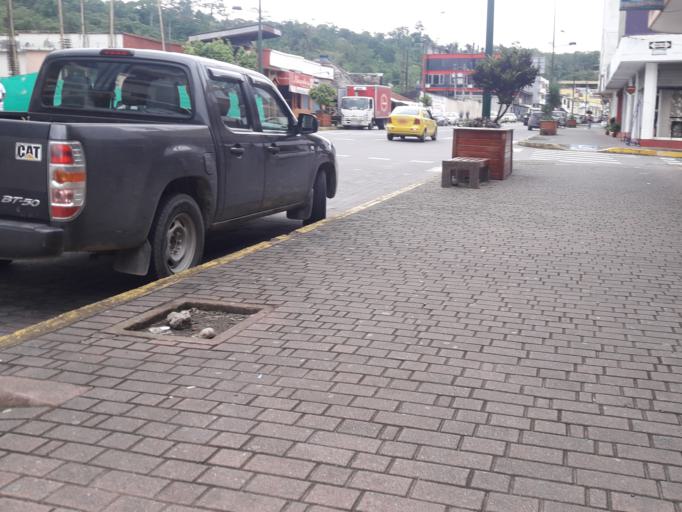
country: EC
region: Napo
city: Tena
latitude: -1.0048
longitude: -77.8106
